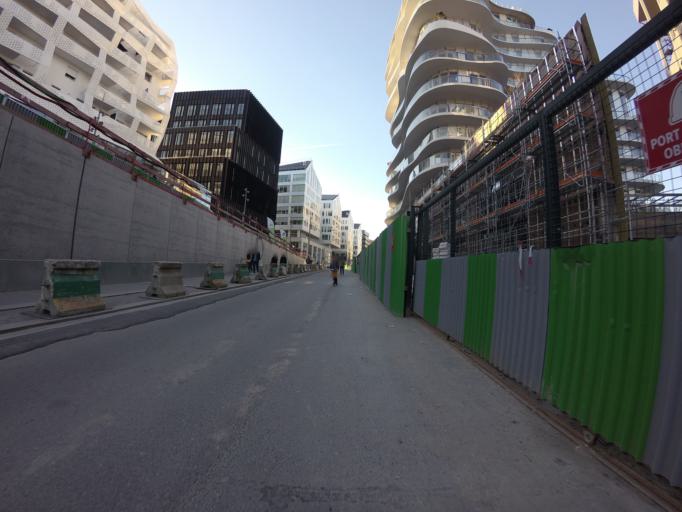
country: FR
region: Ile-de-France
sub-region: Departement des Hauts-de-Seine
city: Clichy
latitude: 48.8890
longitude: 2.3144
